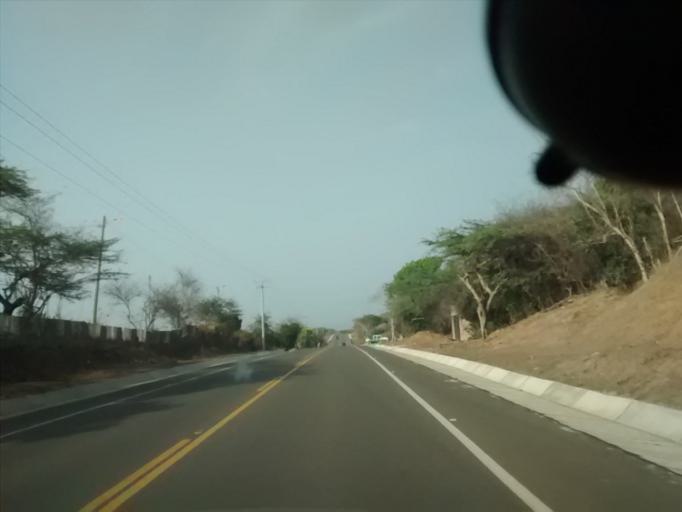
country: CO
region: Atlantico
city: Juan de Acosta
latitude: 10.8723
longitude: -75.0863
